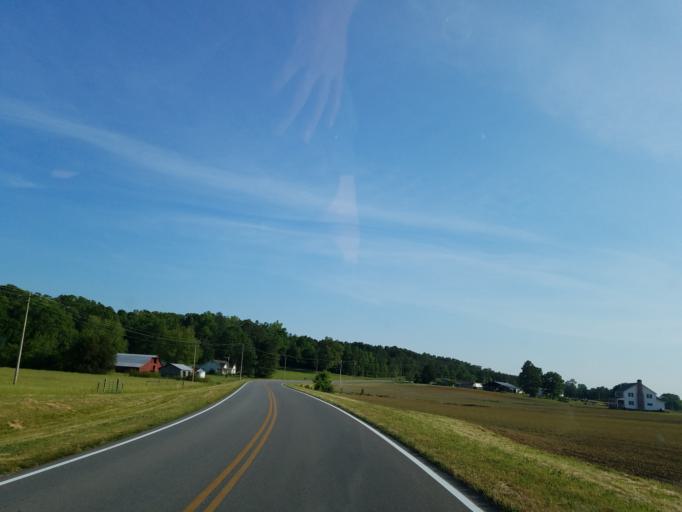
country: US
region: Georgia
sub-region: Chattooga County
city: Trion
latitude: 34.5155
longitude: -85.2309
